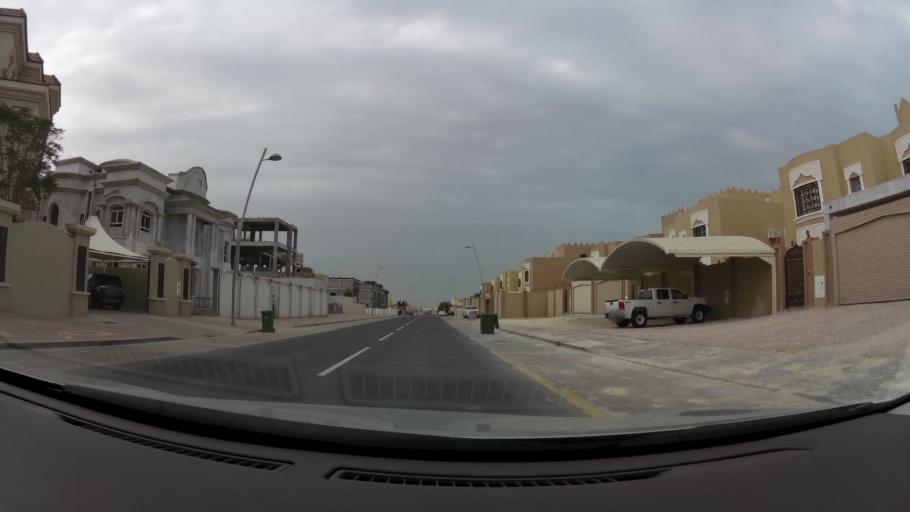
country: QA
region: Baladiyat ad Dawhah
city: Doha
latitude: 25.3388
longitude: 51.4880
